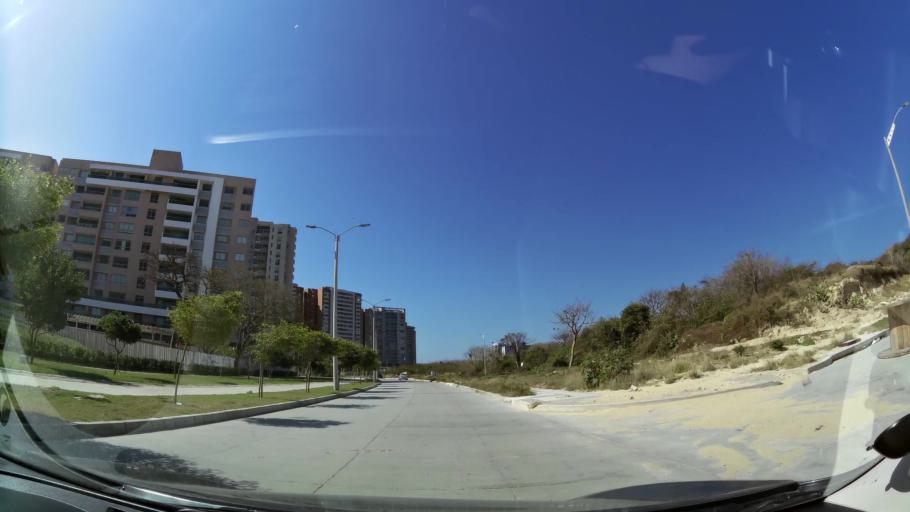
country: CO
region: Atlantico
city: Barranquilla
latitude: 11.0207
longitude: -74.8259
